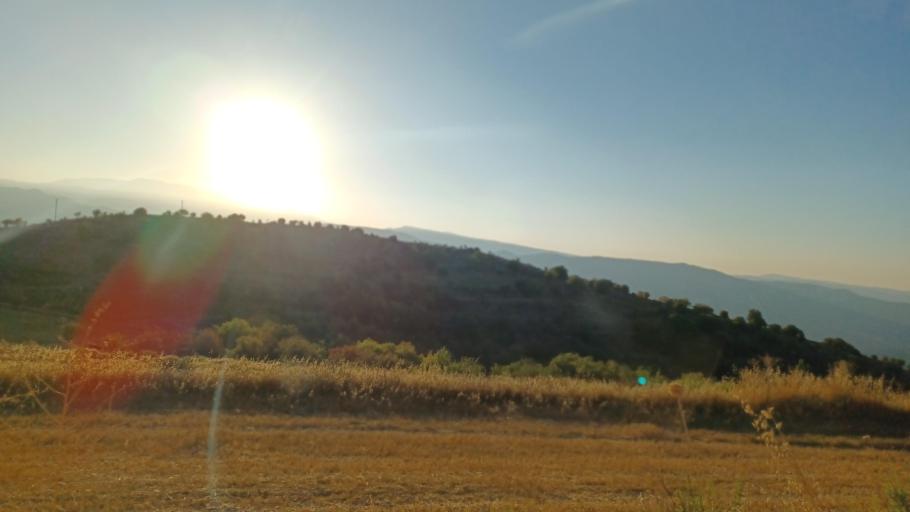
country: CY
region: Pafos
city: Mesogi
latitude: 34.8639
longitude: 32.6215
